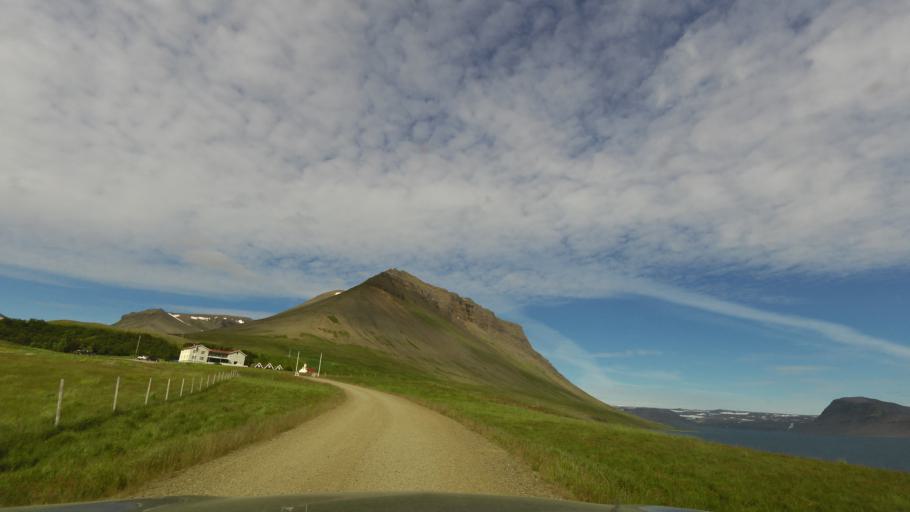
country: IS
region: Westfjords
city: Isafjoerdur
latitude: 65.7579
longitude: -23.4548
